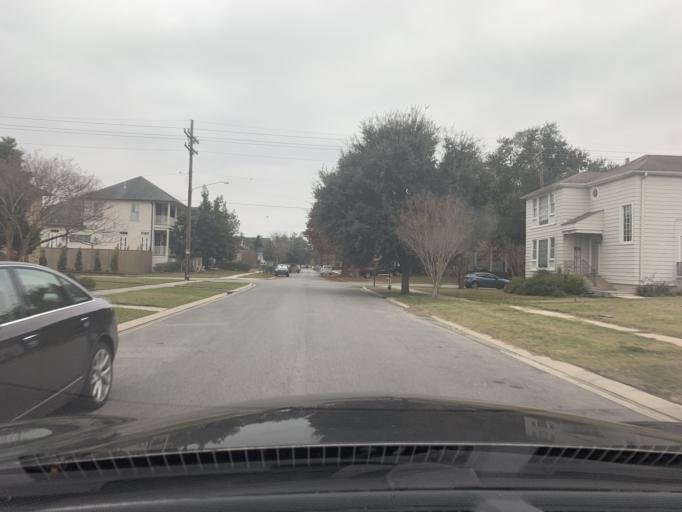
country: US
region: Louisiana
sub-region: Jefferson Parish
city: Metairie
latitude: 30.0147
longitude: -90.1092
